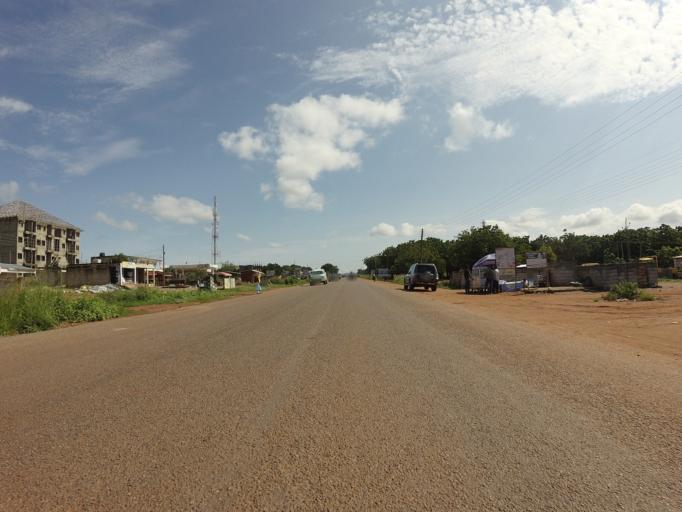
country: GH
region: Eastern
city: Aburi
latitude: 5.8045
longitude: -0.1254
